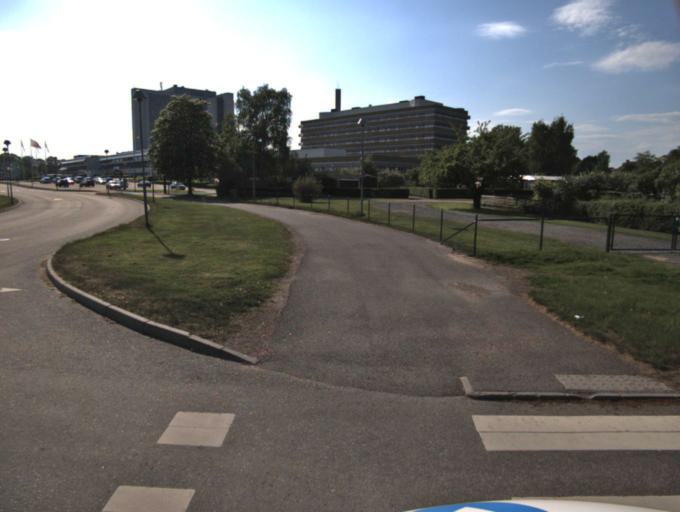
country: SE
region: Skane
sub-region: Kristianstads Kommun
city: Kristianstad
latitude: 56.0306
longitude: 14.1784
